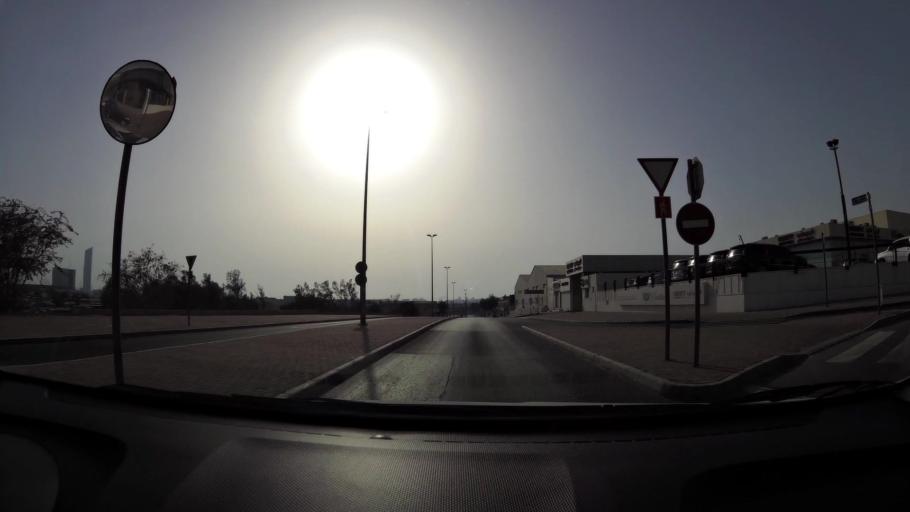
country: AE
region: Ash Shariqah
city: Sharjah
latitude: 25.2360
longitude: 55.3682
